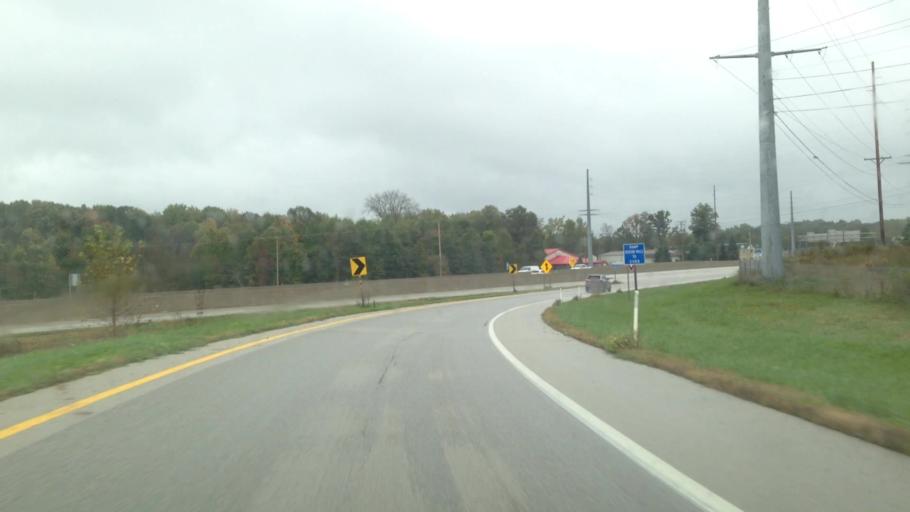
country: US
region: Ohio
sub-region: Summit County
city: Boston Heights
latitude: 41.2530
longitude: -81.5006
